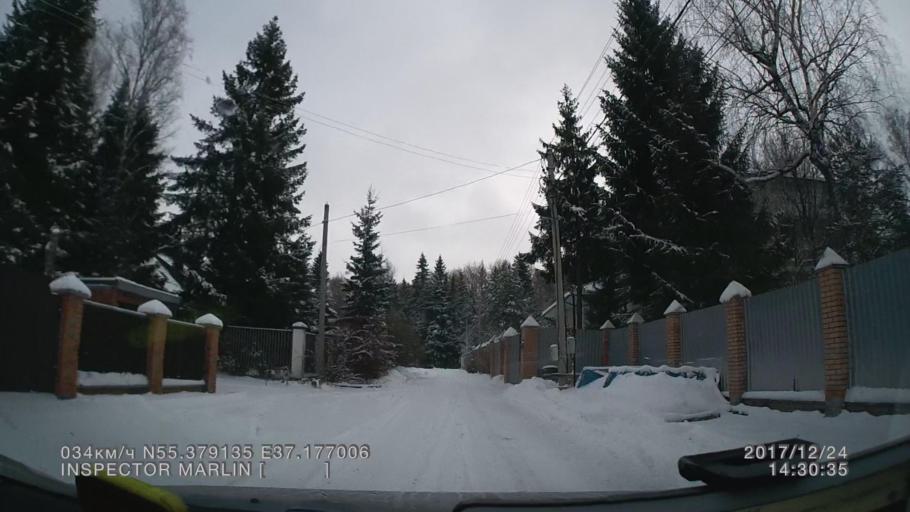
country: RU
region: Moskovskaya
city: Troitsk
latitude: 55.3791
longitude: 37.1773
